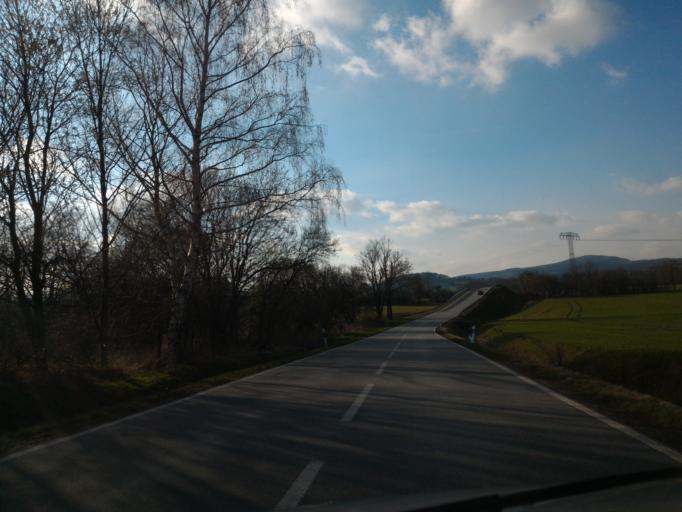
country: DE
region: Saxony
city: Grossschonau
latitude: 50.8893
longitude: 14.6909
